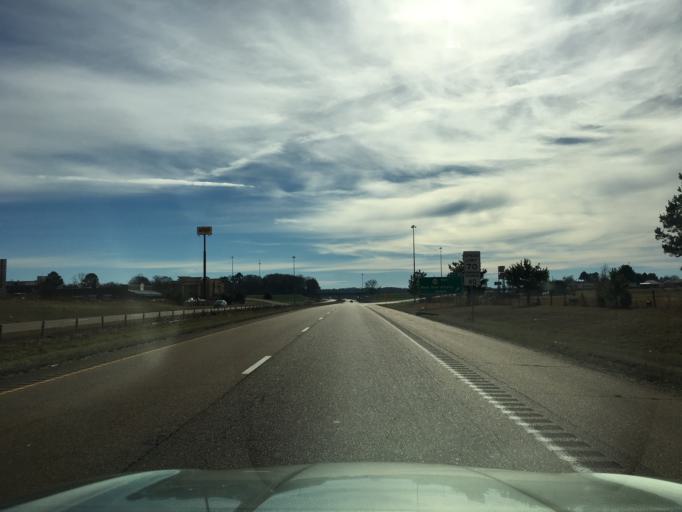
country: US
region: Mississippi
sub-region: Union County
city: New Albany
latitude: 34.5015
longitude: -89.0347
